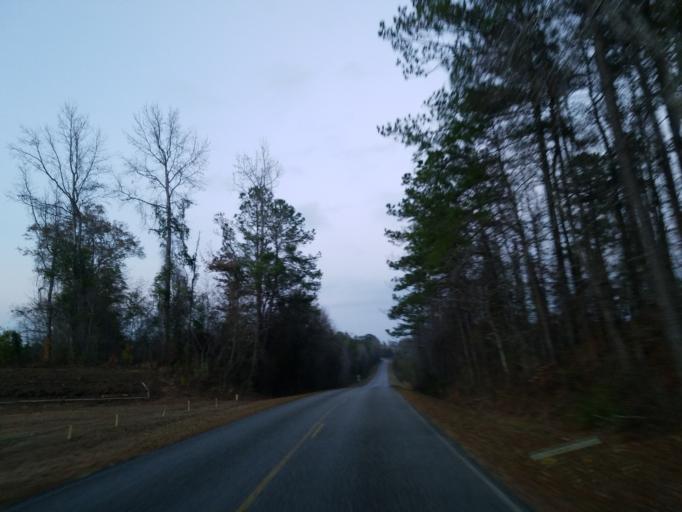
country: US
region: Alabama
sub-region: Sumter County
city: York
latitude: 32.4068
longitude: -88.4427
